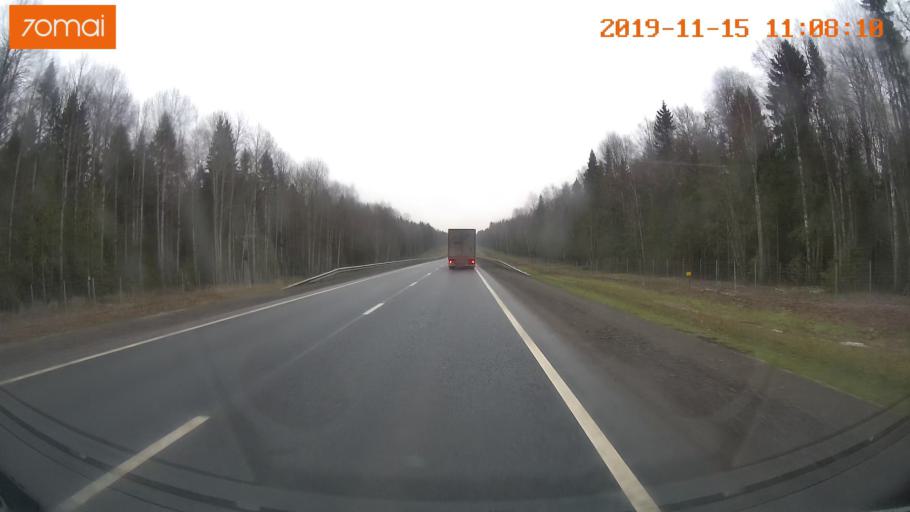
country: RU
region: Vologda
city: Chebsara
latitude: 59.1198
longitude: 39.0677
